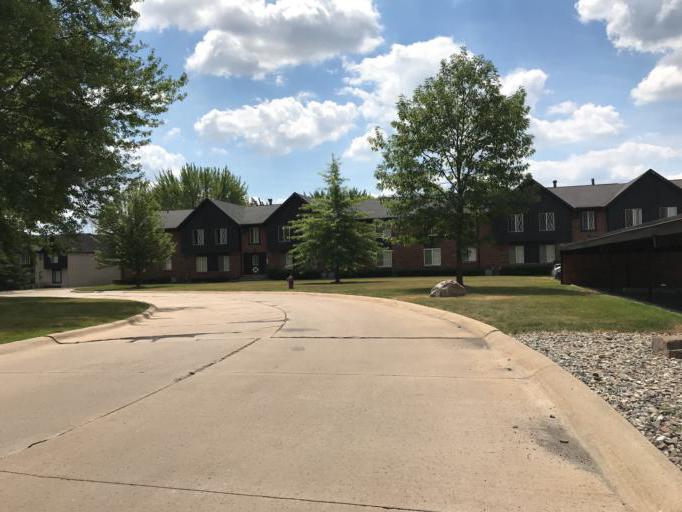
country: US
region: Michigan
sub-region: Oakland County
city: Bingham Farms
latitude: 42.5035
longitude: -83.2895
